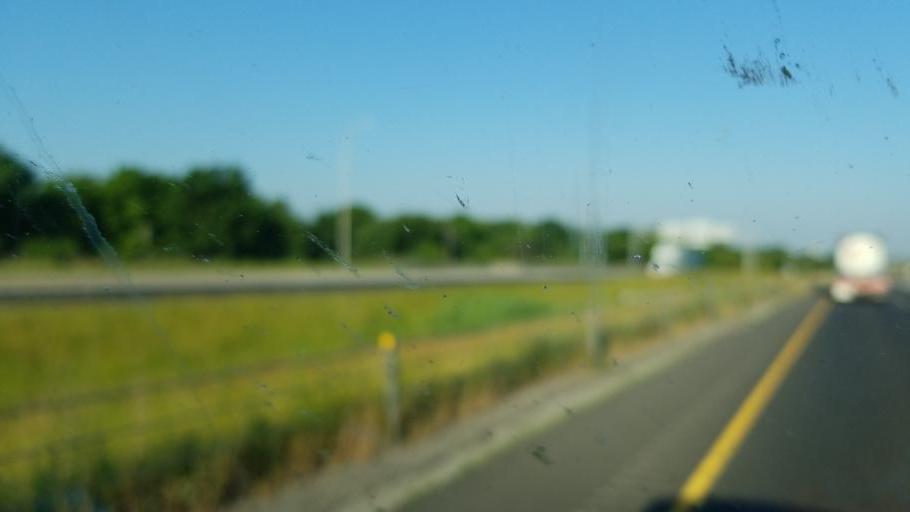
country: US
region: Illinois
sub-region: Will County
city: Shorewood
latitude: 41.4861
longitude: -88.2027
